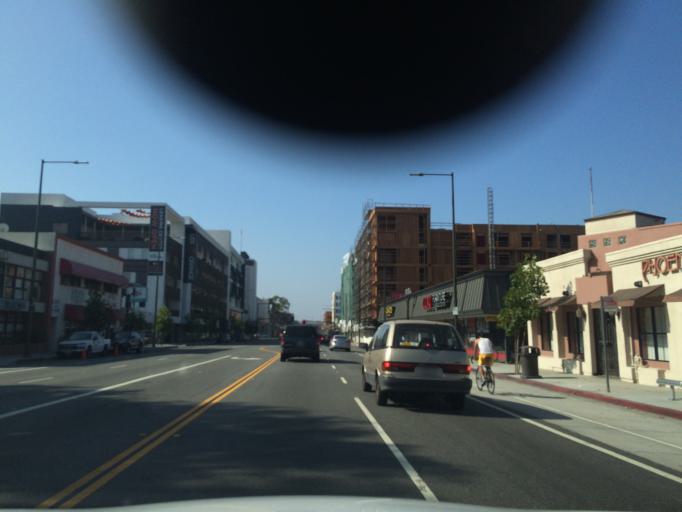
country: US
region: California
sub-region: Los Angeles County
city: Glendale
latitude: 34.1516
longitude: -118.2580
